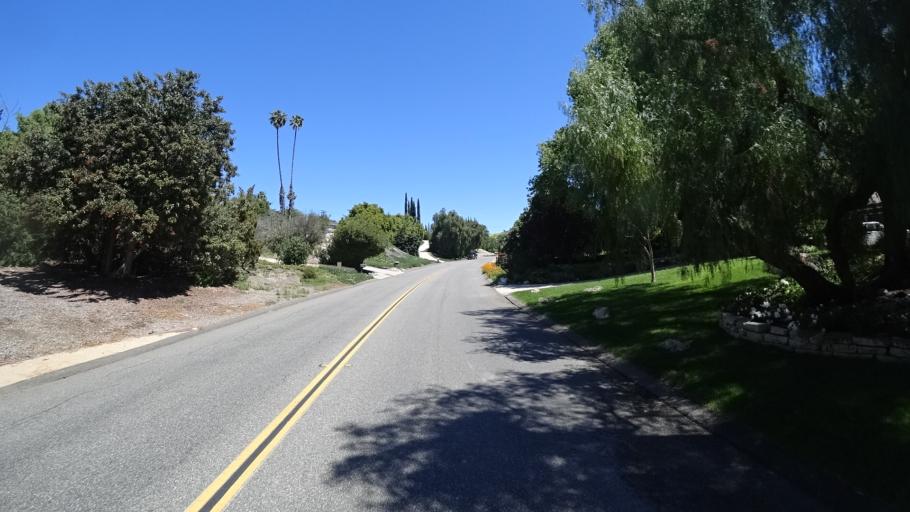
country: US
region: California
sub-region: Ventura County
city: Thousand Oaks
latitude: 34.1925
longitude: -118.8542
